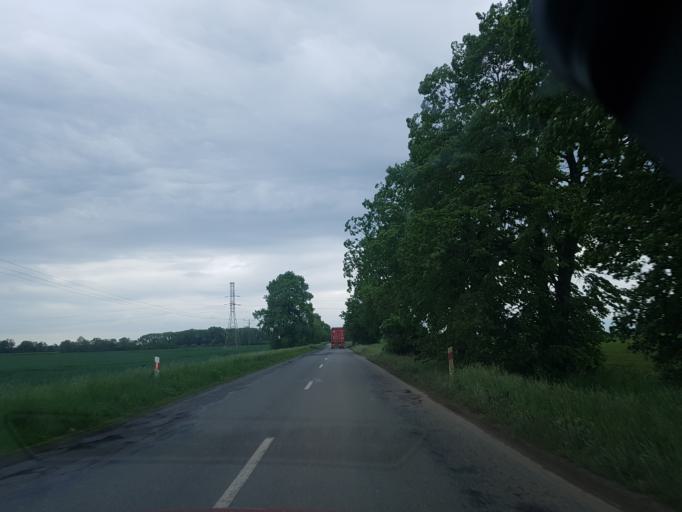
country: PL
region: Lower Silesian Voivodeship
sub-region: Powiat wroclawski
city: Zorawina
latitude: 50.9217
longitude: 17.0163
